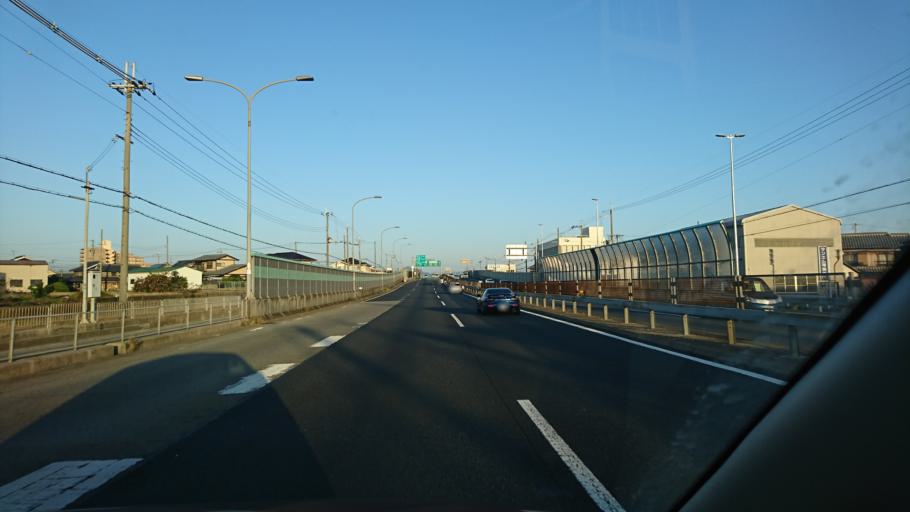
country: JP
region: Hyogo
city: Kakogawacho-honmachi
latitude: 34.7528
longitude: 134.8646
